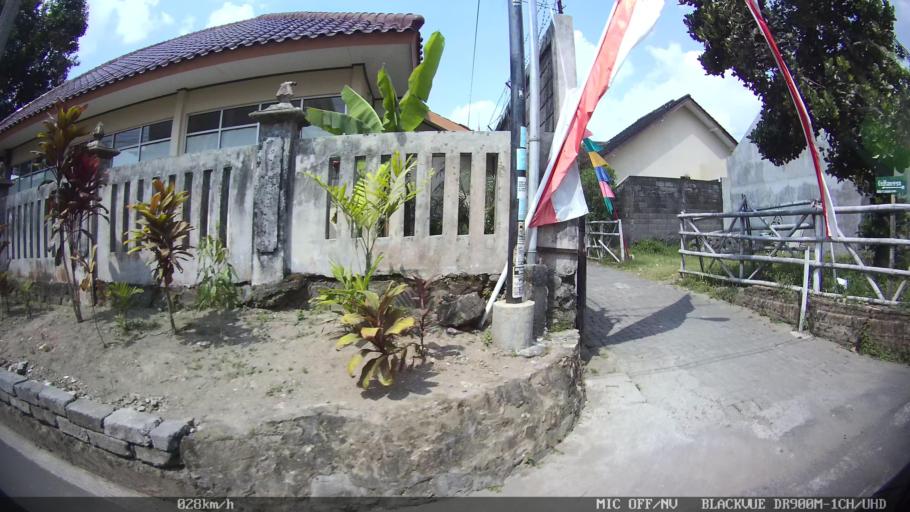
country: ID
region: Daerah Istimewa Yogyakarta
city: Depok
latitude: -7.8004
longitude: 110.4077
